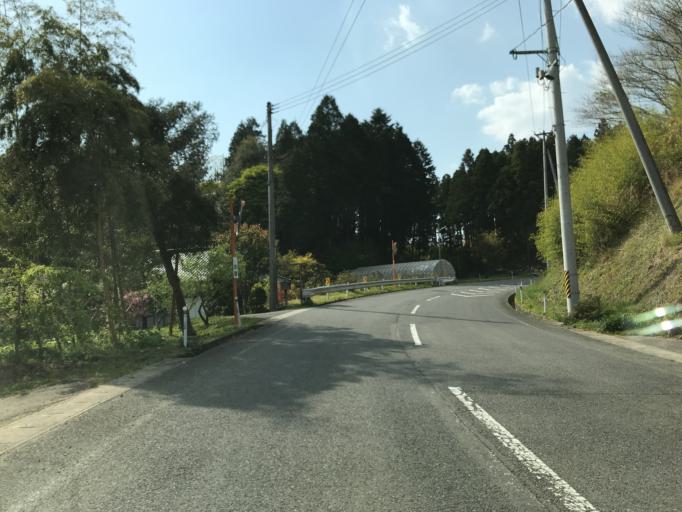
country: JP
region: Fukushima
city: Iwaki
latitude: 36.9998
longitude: 140.7725
